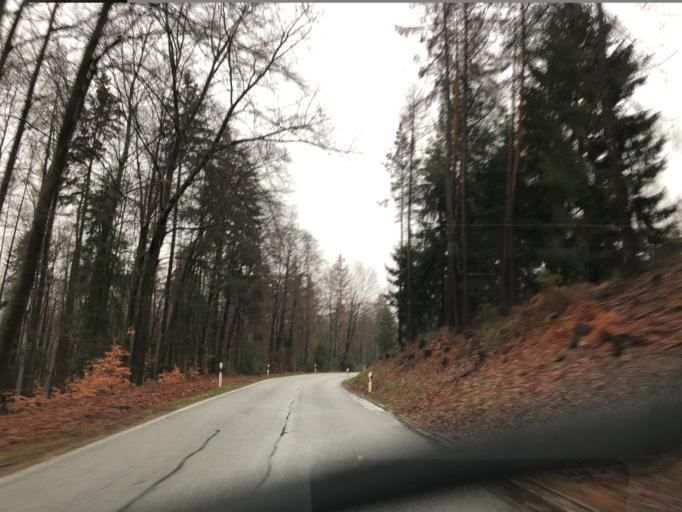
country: DE
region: Hesse
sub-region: Regierungsbezirk Darmstadt
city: Lutzelbach
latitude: 49.7488
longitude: 9.0813
